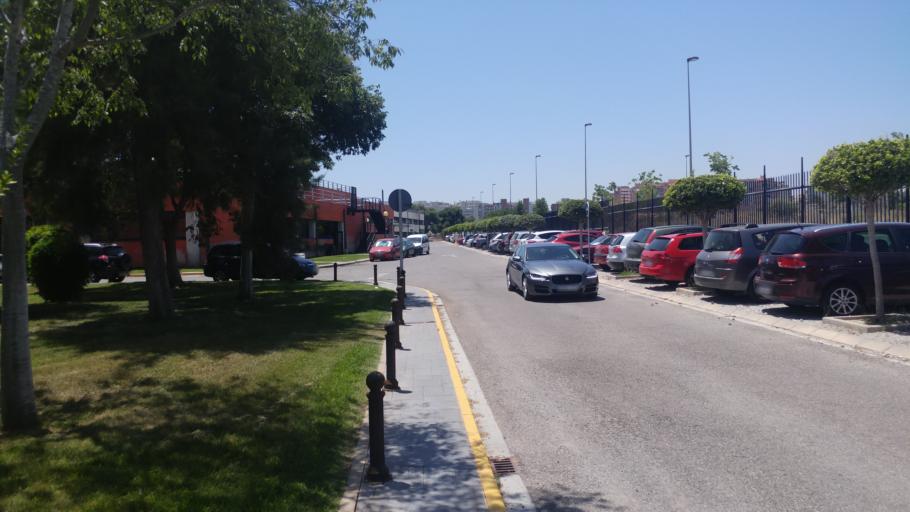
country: ES
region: Valencia
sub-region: Provincia de Valencia
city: Burjassot
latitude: 39.5159
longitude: -0.4247
